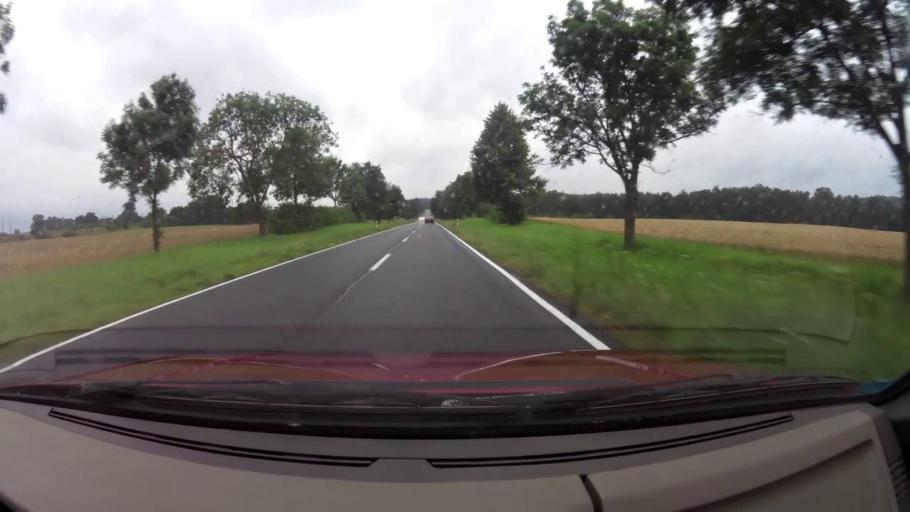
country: PL
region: West Pomeranian Voivodeship
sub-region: Powiat stargardzki
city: Marianowo
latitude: 53.4287
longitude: 15.2897
